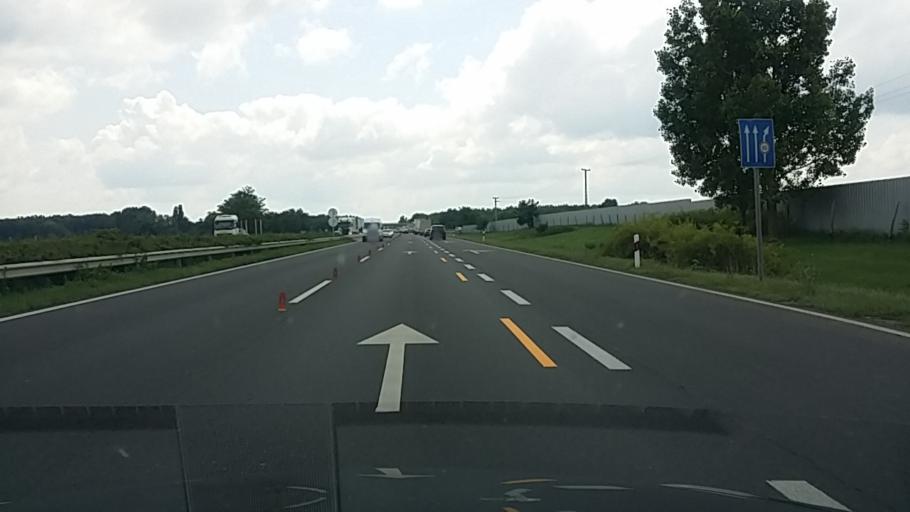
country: HU
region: Pest
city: Hernad
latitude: 47.1528
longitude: 19.4581
